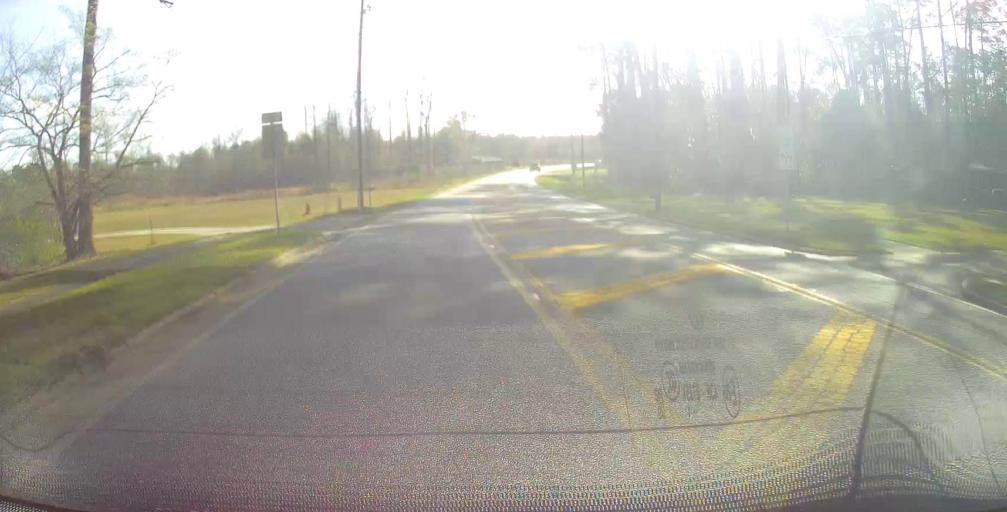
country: US
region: Georgia
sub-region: Montgomery County
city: Mount Vernon
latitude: 32.1755
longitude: -82.6769
